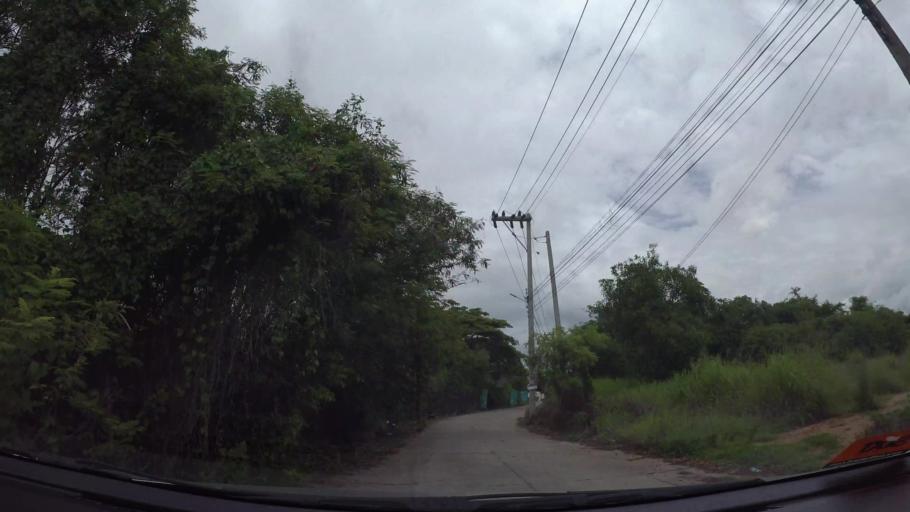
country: TH
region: Chon Buri
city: Si Racha
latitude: 13.1587
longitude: 100.9799
